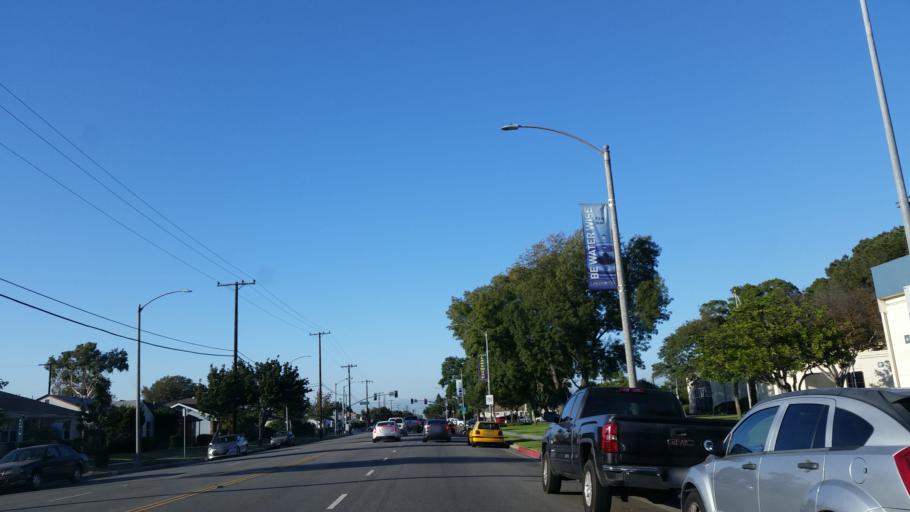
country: US
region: California
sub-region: Los Angeles County
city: Lakewood
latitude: 33.8588
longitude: -118.1337
